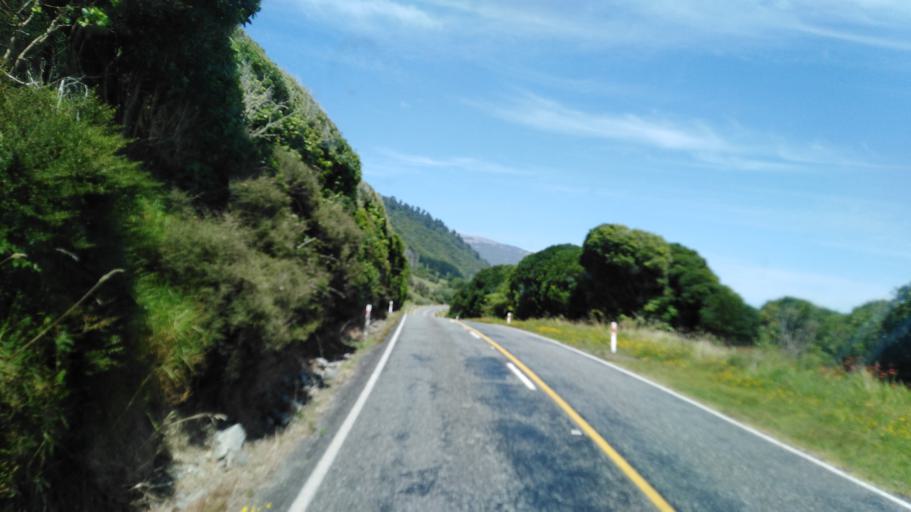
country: NZ
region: West Coast
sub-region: Buller District
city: Westport
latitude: -41.5770
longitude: 171.9004
